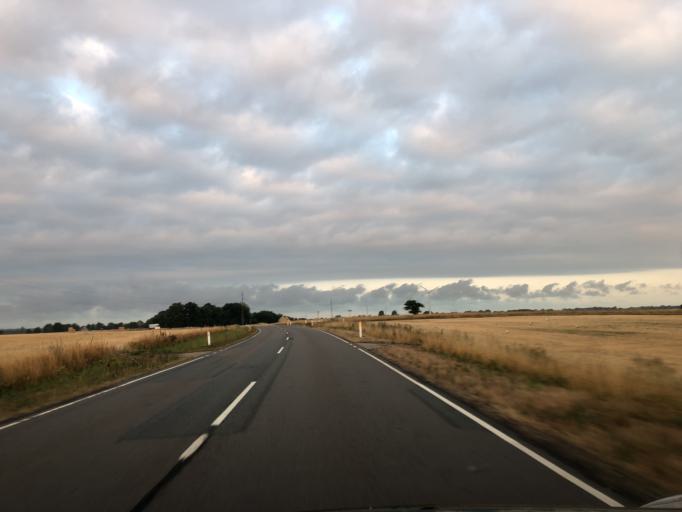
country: DK
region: Zealand
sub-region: Soro Kommune
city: Dianalund
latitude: 55.4538
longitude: 11.4378
